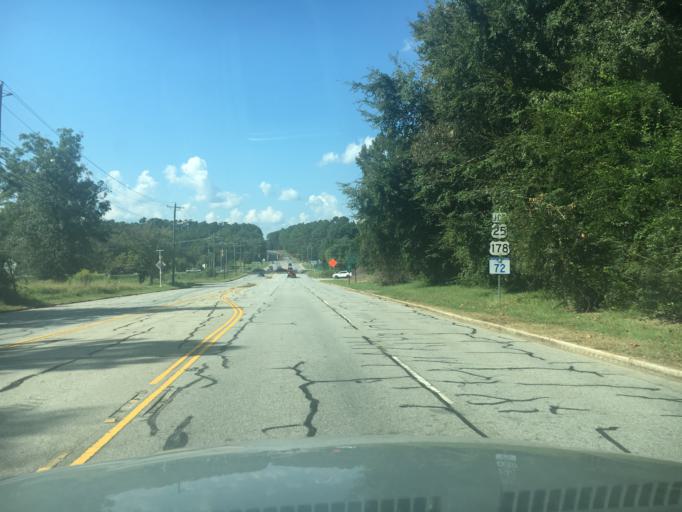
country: US
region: South Carolina
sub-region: Greenwood County
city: Greenwood
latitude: 34.2146
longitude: -82.1675
